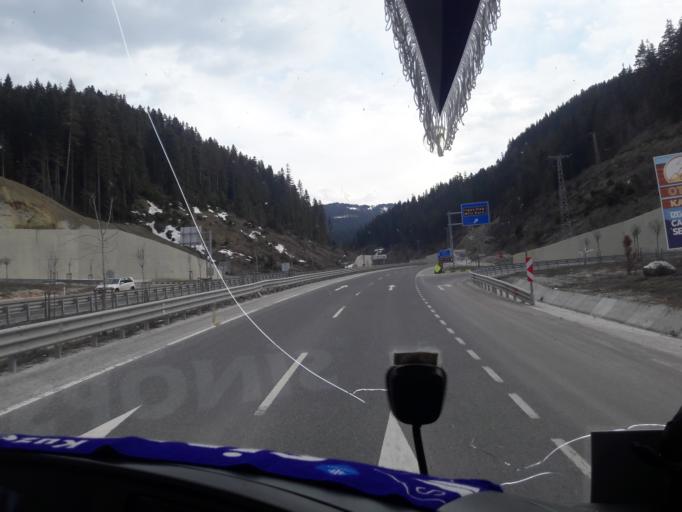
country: TR
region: Kastamonu
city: Kuzyaka
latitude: 41.0998
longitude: 33.7511
